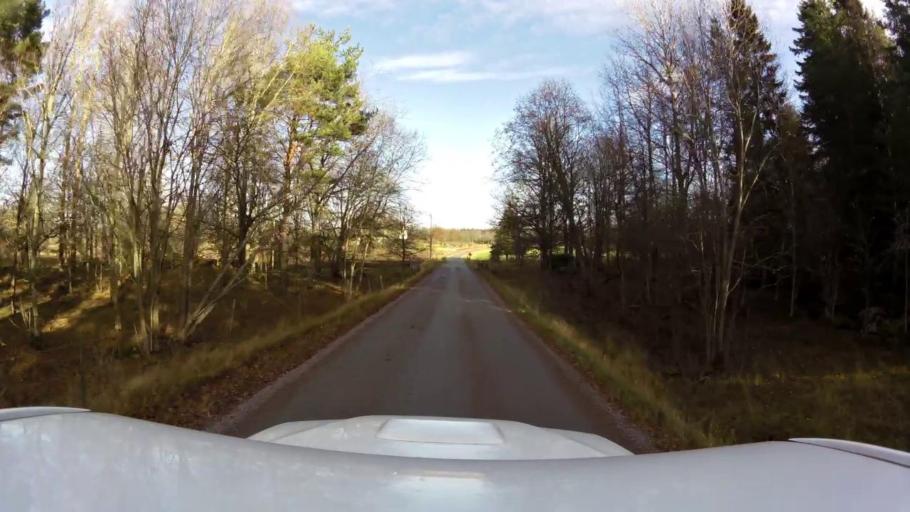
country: SE
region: OEstergoetland
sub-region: Linkopings Kommun
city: Linkoping
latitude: 58.3658
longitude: 15.6061
